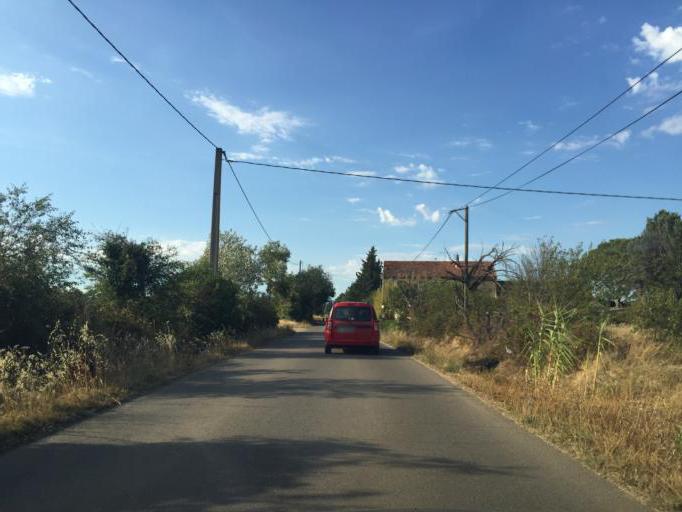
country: FR
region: Provence-Alpes-Cote d'Azur
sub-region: Departement du Vaucluse
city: Pernes-les-Fontaines
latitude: 44.0163
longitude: 5.0550
